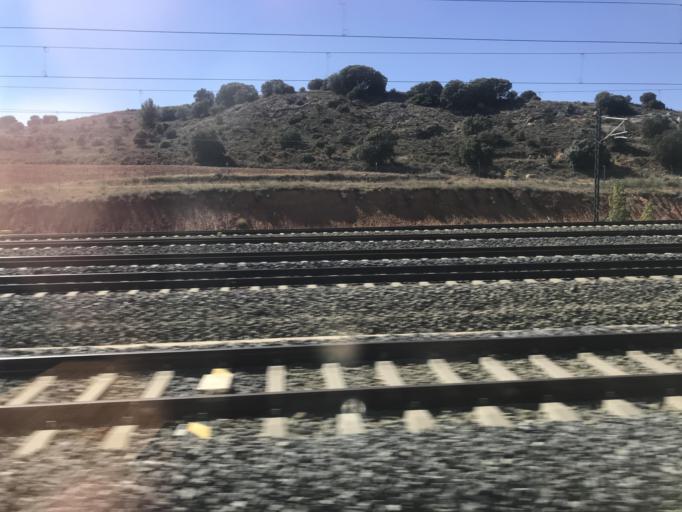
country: ES
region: Castille-La Mancha
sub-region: Provincia de Cuenca
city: Cuenca
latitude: 40.0323
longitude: -2.1411
